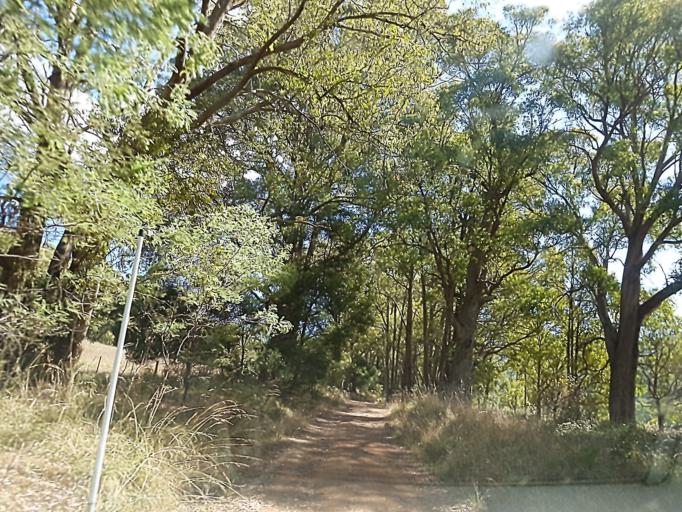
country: AU
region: Victoria
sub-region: Alpine
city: Mount Beauty
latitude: -36.8745
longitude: 147.0564
